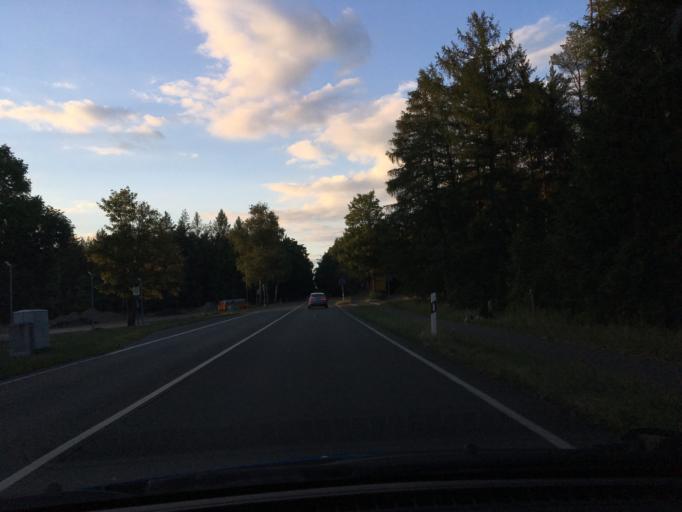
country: DE
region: Lower Saxony
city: Bergen
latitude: 52.7464
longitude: 9.9778
